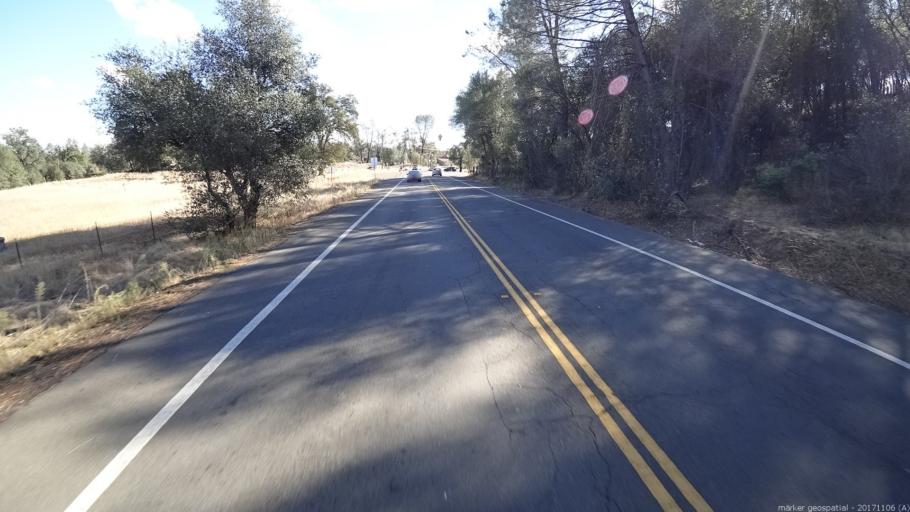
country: US
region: California
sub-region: Shasta County
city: Palo Cedro
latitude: 40.5892
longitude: -122.3074
